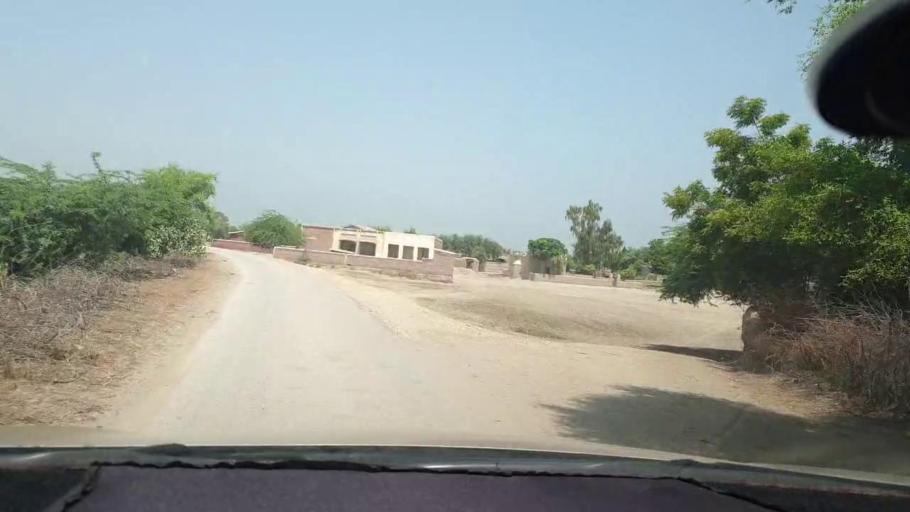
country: PK
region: Sindh
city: Kambar
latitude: 27.6649
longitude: 67.9152
